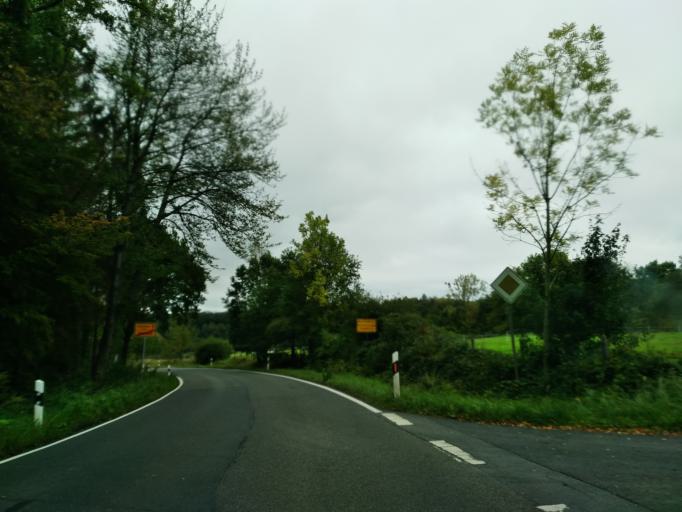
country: DE
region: North Rhine-Westphalia
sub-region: Regierungsbezirk Koln
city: Bad Honnef
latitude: 50.6783
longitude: 7.2718
